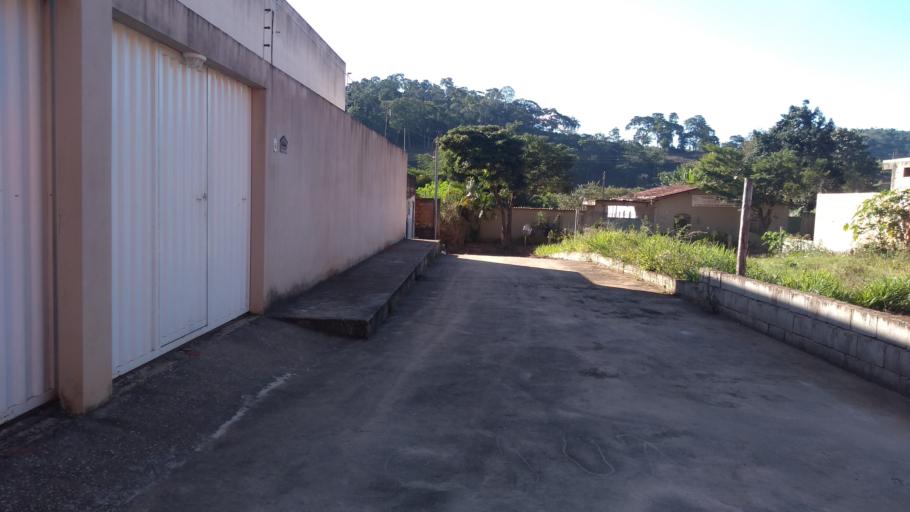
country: BR
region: Minas Gerais
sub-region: Teofilo Otoni
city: Teofilo Otoni
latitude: -17.8724
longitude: -41.5290
